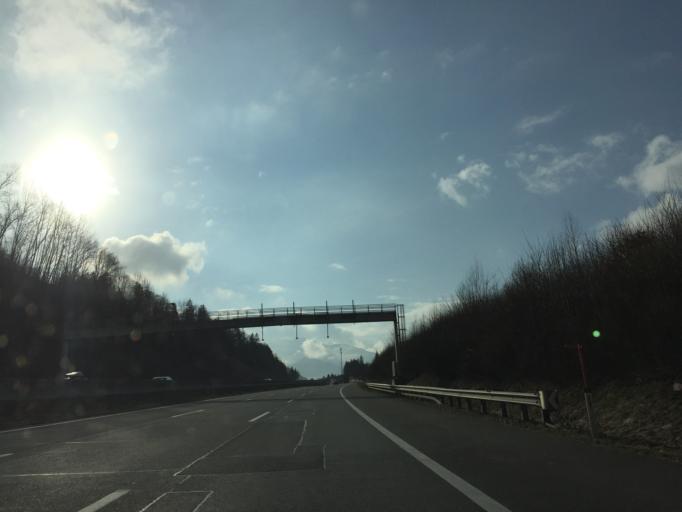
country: AT
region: Salzburg
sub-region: Politischer Bezirk Sankt Johann im Pongau
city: Pfarrwerfen
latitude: 47.4658
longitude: 13.2036
